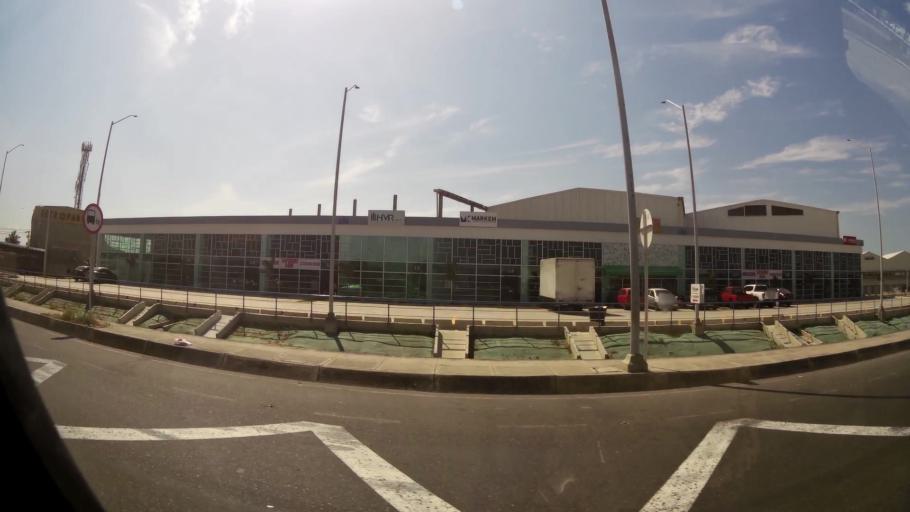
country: CO
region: Atlantico
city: Barranquilla
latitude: 10.9481
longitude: -74.8339
